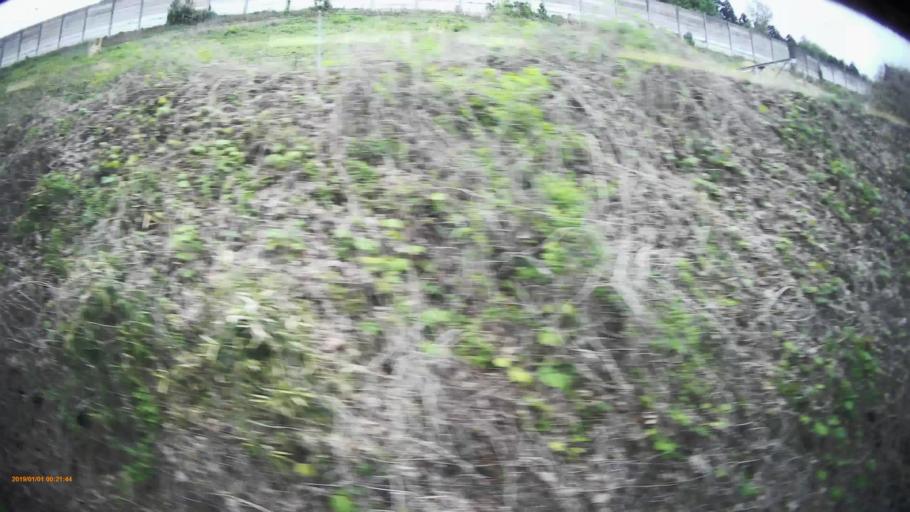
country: JP
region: Yamanashi
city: Uenohara
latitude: 35.6151
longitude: 139.1588
